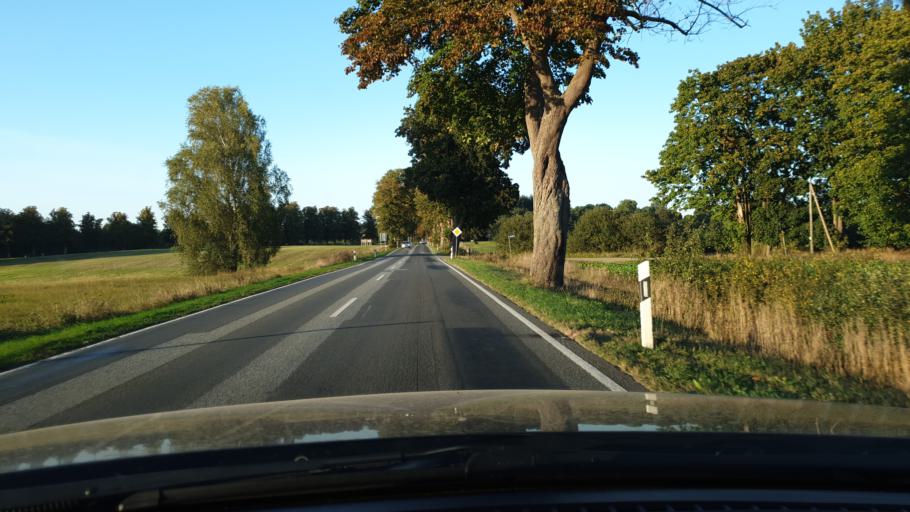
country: DE
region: Mecklenburg-Vorpommern
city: Wittenburg
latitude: 53.5699
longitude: 11.1000
